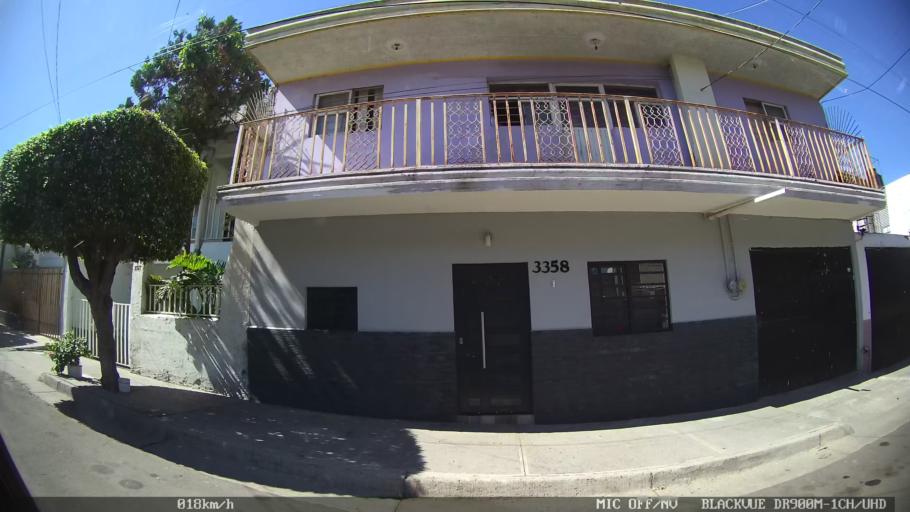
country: MX
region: Jalisco
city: Tlaquepaque
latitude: 20.6991
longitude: -103.2818
